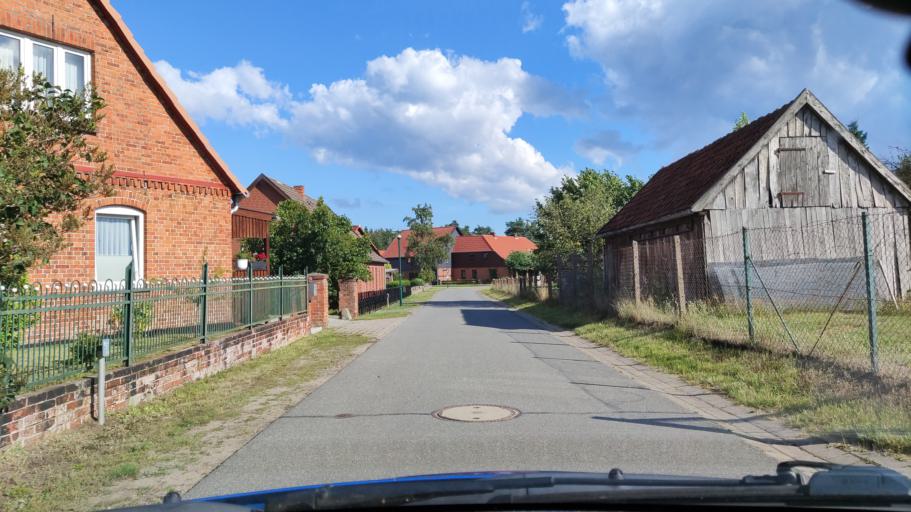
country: DE
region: Lower Saxony
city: Neu Darchau
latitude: 53.2819
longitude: 10.9340
